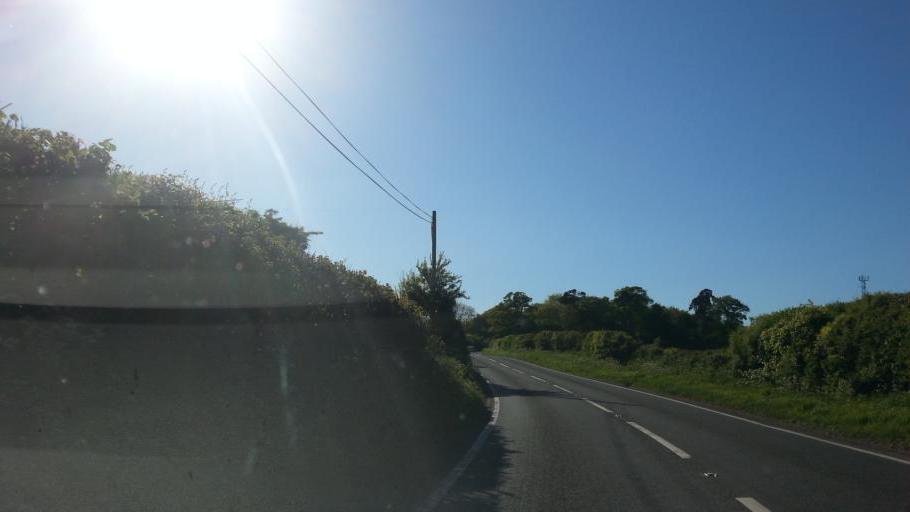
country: GB
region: England
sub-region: Somerset
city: Wincanton
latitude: 51.0573
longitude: -2.4521
